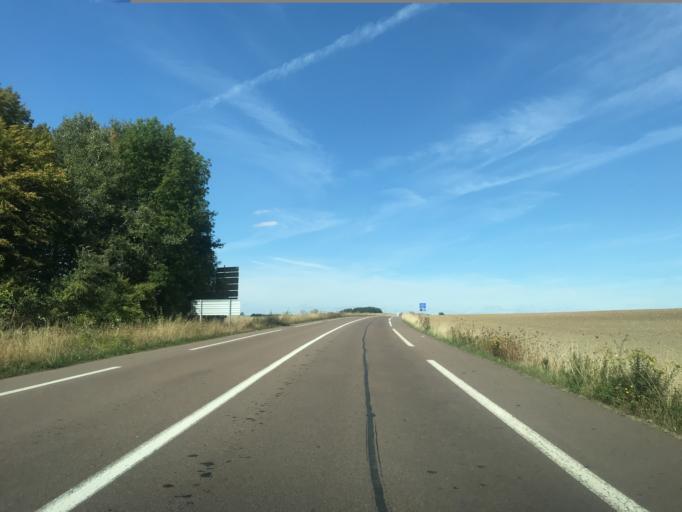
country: FR
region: Champagne-Ardenne
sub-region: Departement de la Marne
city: Chatillon-sur-Marne
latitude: 49.1484
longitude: 3.7142
